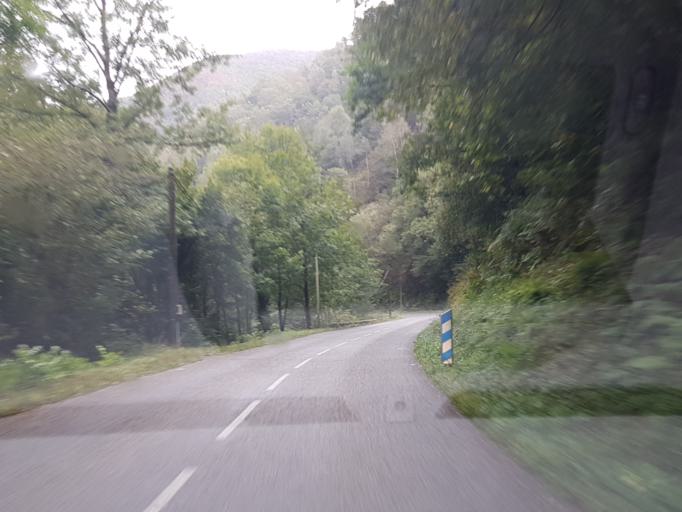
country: FR
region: Midi-Pyrenees
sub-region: Departement de l'Ariege
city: Saint-Girons
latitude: 42.9118
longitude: 1.2688
